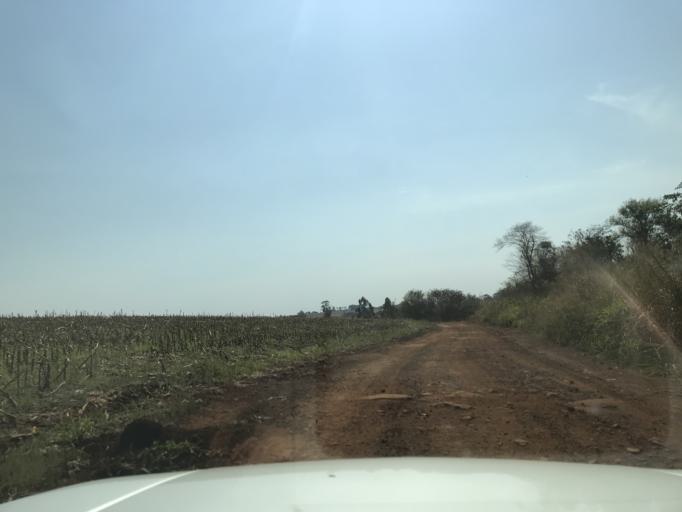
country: BR
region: Parana
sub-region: Palotina
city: Palotina
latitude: -24.2184
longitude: -53.7328
